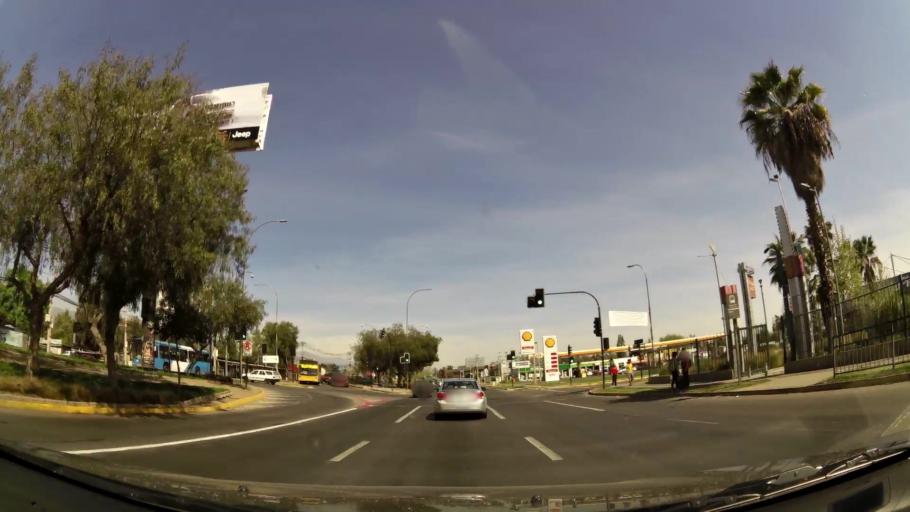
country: CL
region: Santiago Metropolitan
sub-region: Provincia de Cordillera
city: Puente Alto
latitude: -33.5704
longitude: -70.5550
